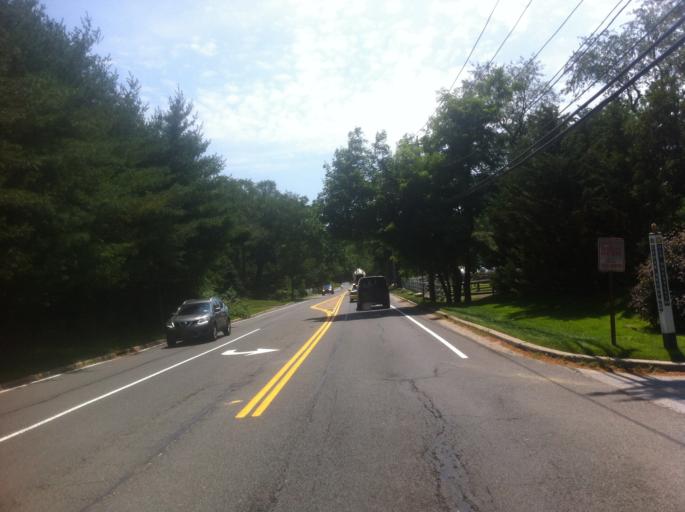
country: US
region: New York
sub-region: Nassau County
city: Old Brookville
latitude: 40.8241
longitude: -73.5861
